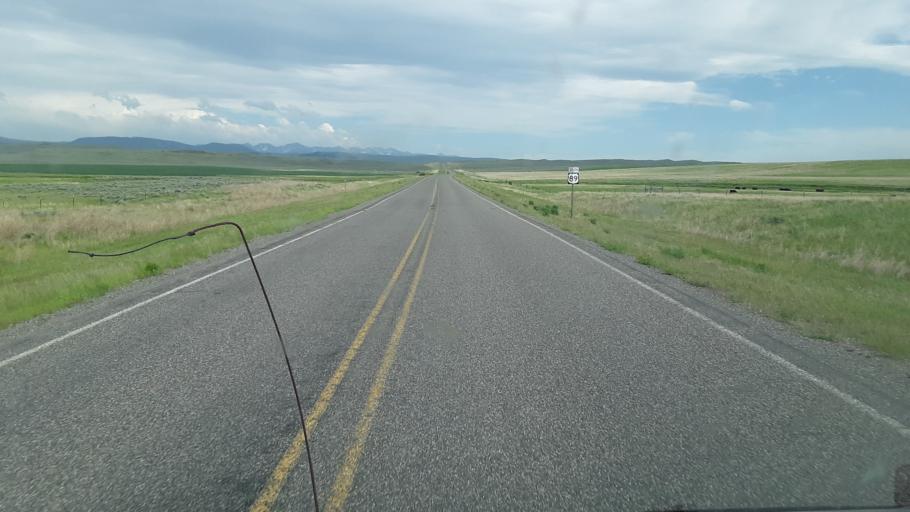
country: US
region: Montana
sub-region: Meagher County
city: White Sulphur Springs
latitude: 46.2699
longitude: -110.8019
